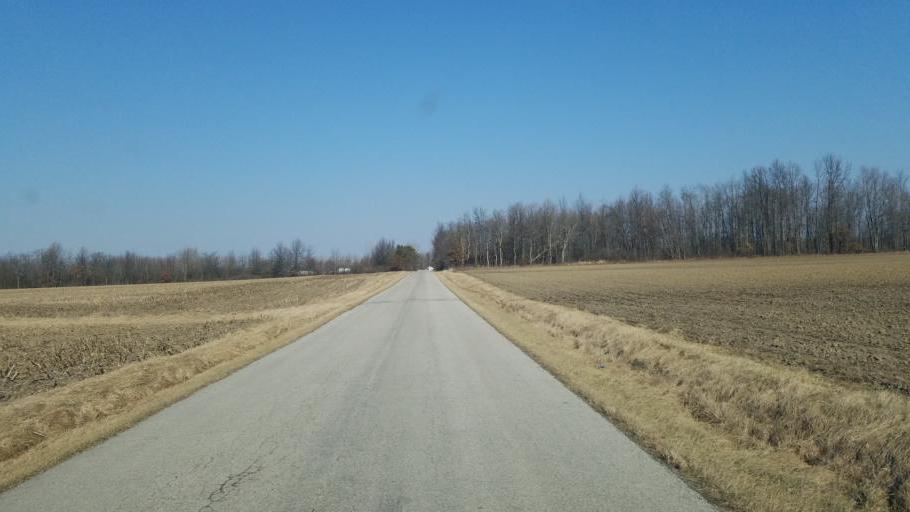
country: US
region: Ohio
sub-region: Crawford County
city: Crestline
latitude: 40.7744
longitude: -82.7651
